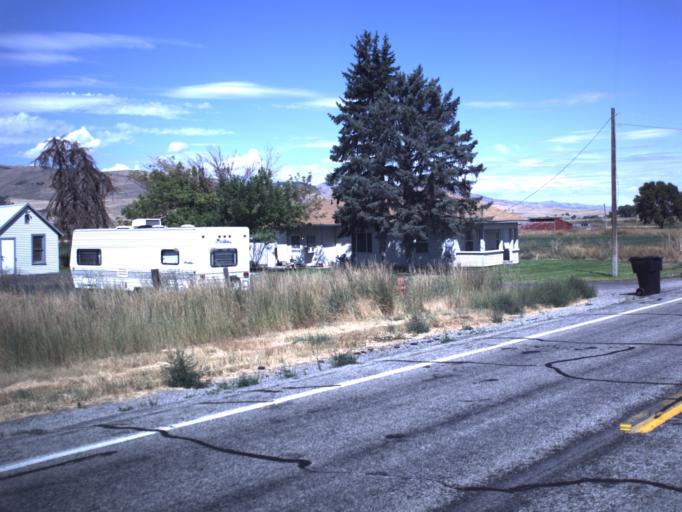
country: US
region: Utah
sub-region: Box Elder County
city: Garland
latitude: 41.7580
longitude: -112.1485
